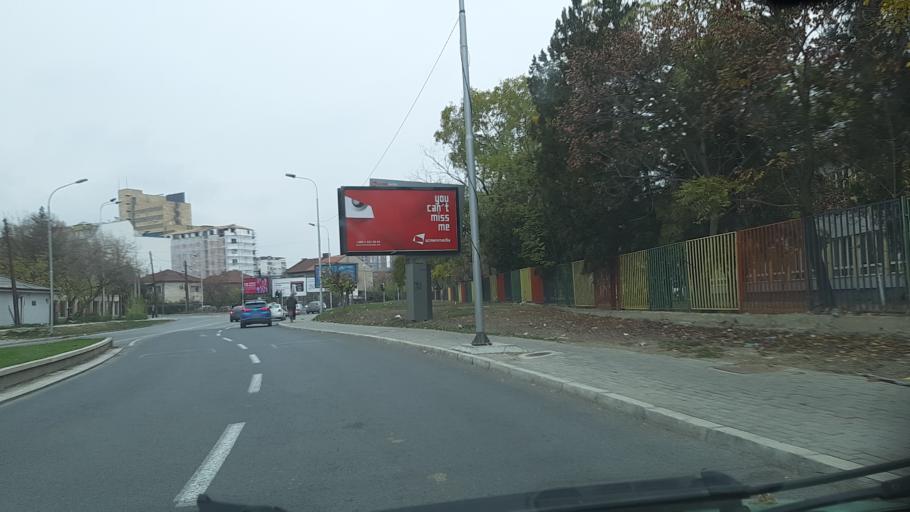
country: MK
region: Karpos
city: Skopje
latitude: 41.9887
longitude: 21.4403
